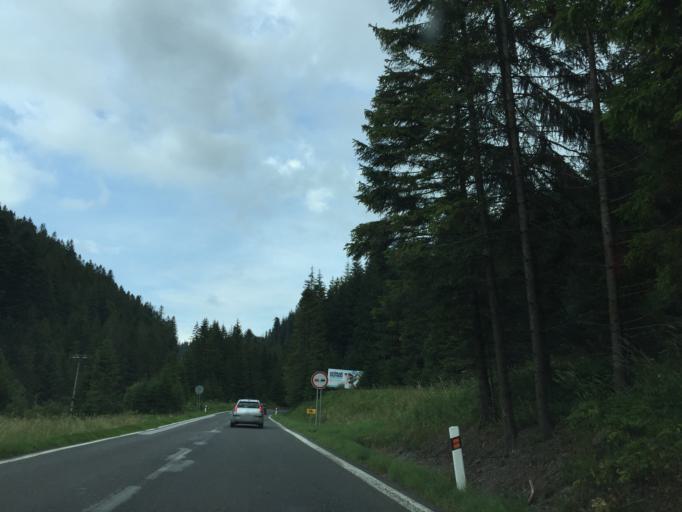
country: SK
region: Presovsky
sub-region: Okres Poprad
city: Zdiar
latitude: 49.2563
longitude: 20.3021
